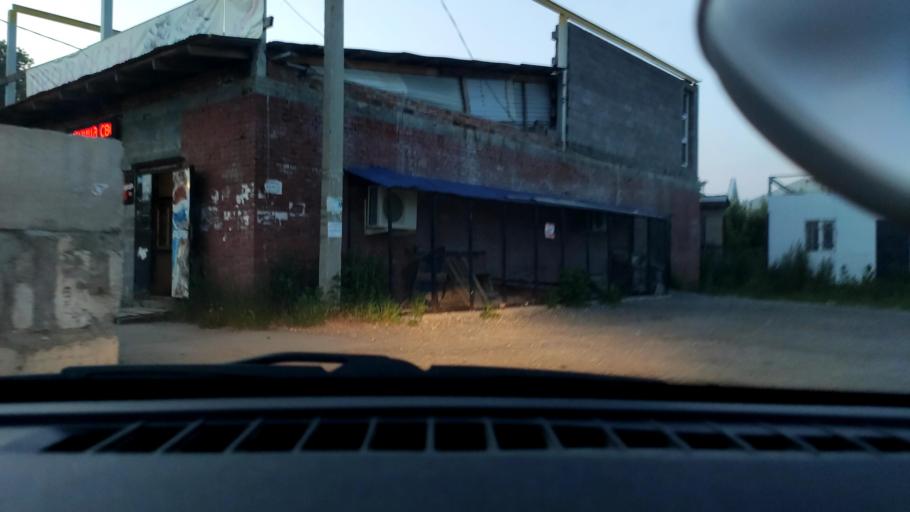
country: RU
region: Samara
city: Novokuybyshevsk
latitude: 53.1472
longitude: 49.9822
